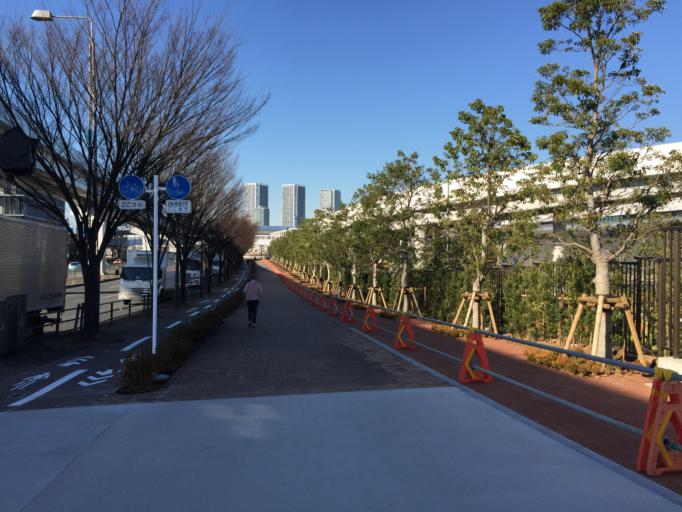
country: JP
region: Tokyo
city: Tokyo
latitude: 35.6434
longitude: 139.7865
